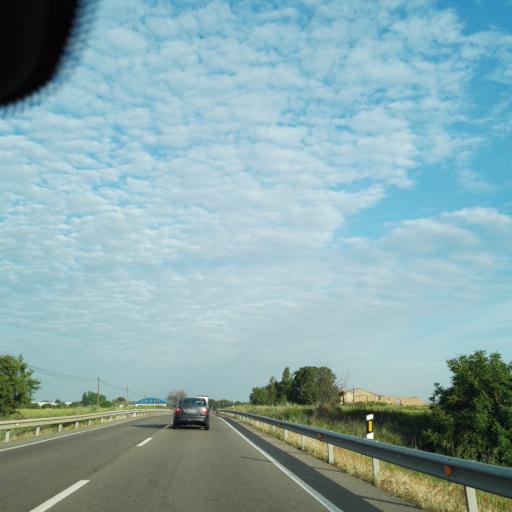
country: ES
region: Aragon
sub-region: Provincia de Zaragoza
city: Oliver-Valdefierro, Oliver, Valdefierro
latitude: 41.6623
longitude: -0.9595
